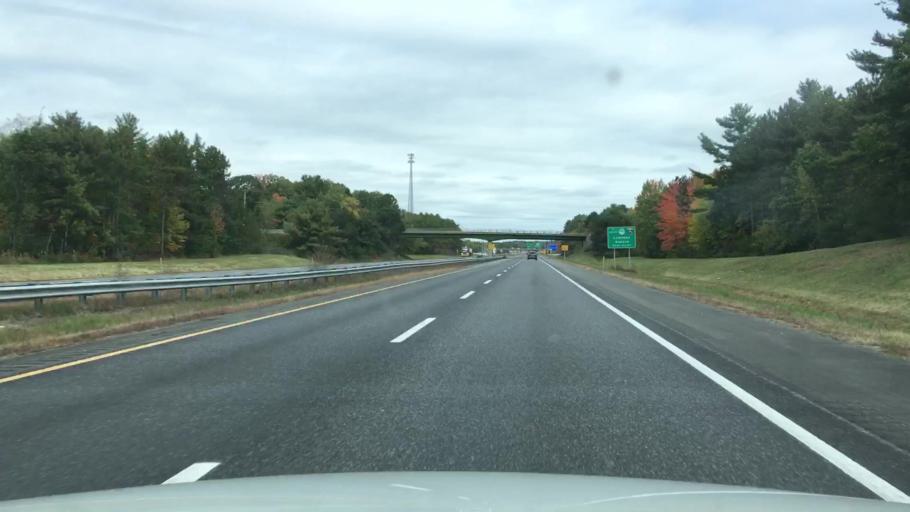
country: US
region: Maine
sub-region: Kennebec County
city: Gardiner
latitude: 44.1992
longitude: -69.8256
